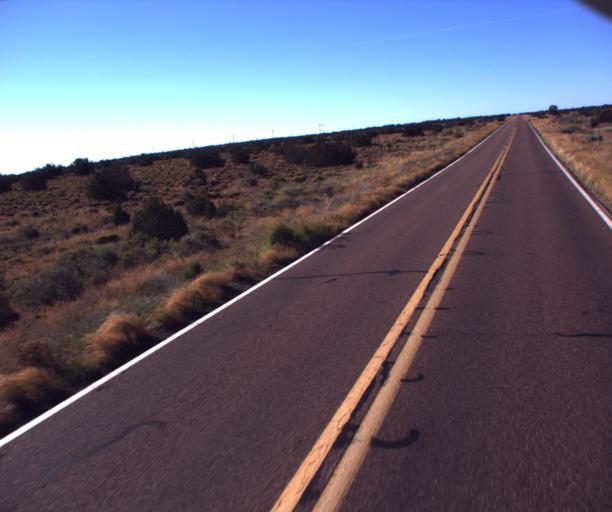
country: US
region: Arizona
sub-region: Navajo County
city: Holbrook
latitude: 34.7020
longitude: -110.3029
